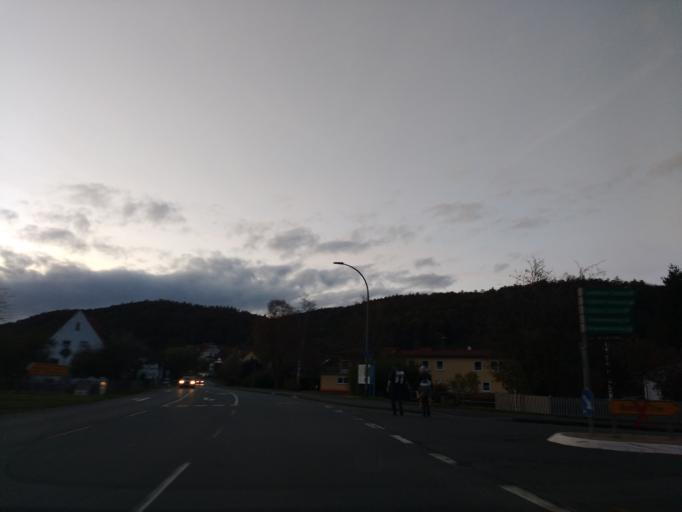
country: DE
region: Hesse
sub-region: Regierungsbezirk Kassel
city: Waldeck
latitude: 51.1677
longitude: 9.0847
